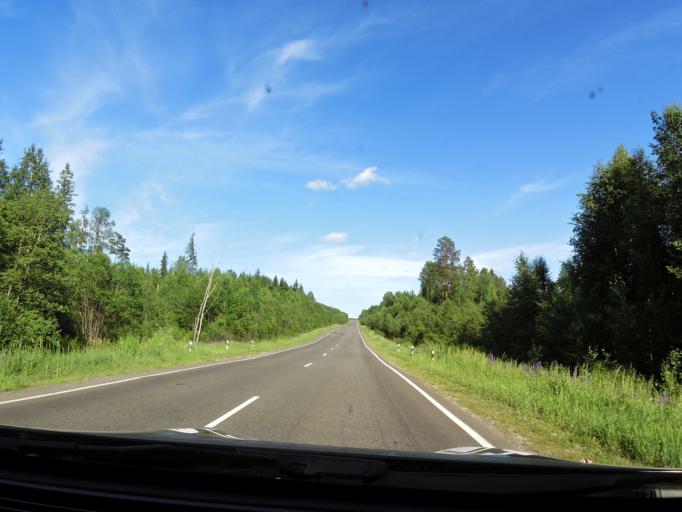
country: RU
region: Kirov
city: Dubrovka
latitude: 58.9015
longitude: 51.2921
